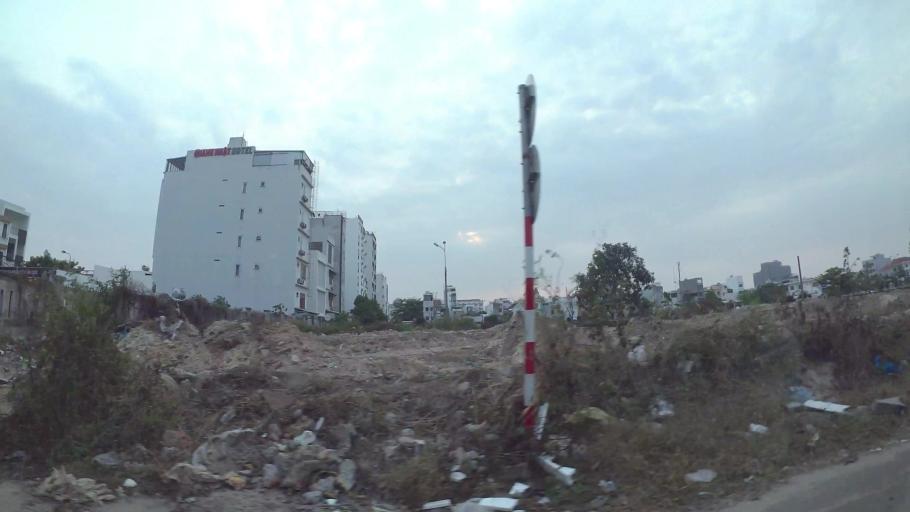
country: VN
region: Da Nang
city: Son Tra
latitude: 16.0490
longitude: 108.2432
